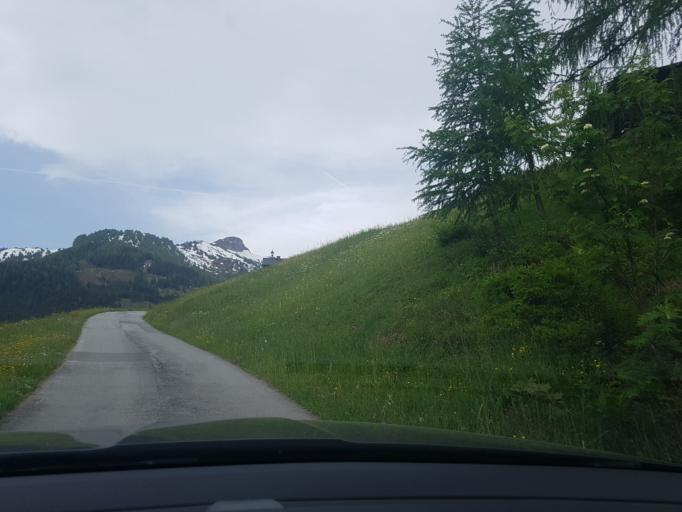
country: AT
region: Salzburg
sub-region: Politischer Bezirk Sankt Johann im Pongau
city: Schwarzach im Pongau
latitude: 47.2758
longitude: 13.1964
